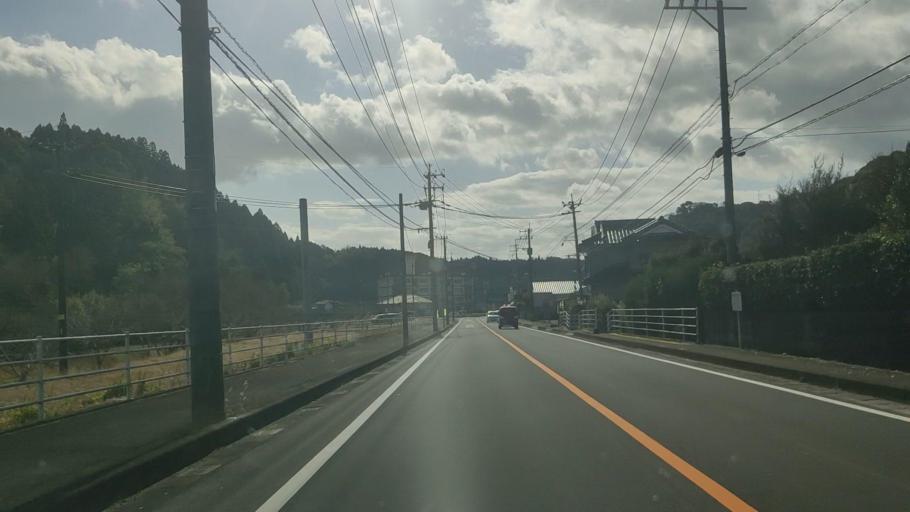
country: JP
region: Kagoshima
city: Okuchi-shinohara
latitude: 31.9444
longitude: 130.7108
